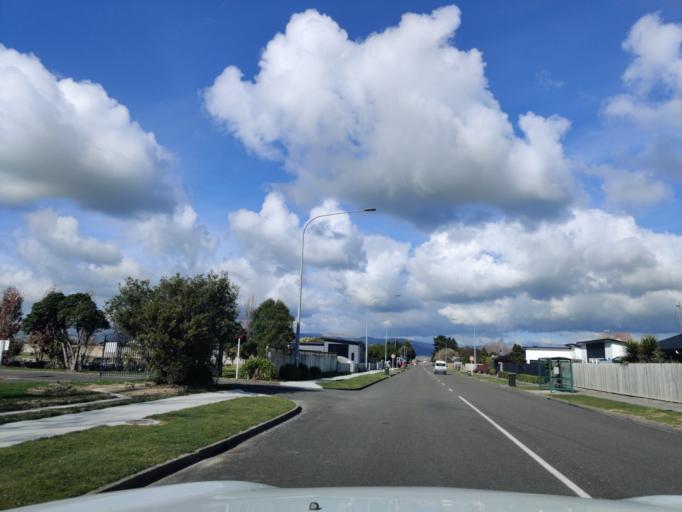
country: NZ
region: Manawatu-Wanganui
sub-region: Palmerston North City
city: Palmerston North
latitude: -40.3249
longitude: 175.6616
